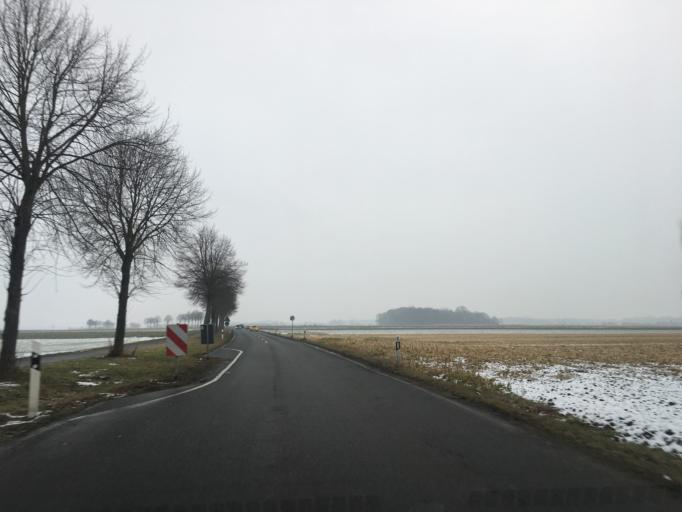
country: DE
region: North Rhine-Westphalia
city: Huckelhoven
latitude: 51.1065
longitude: 6.2390
